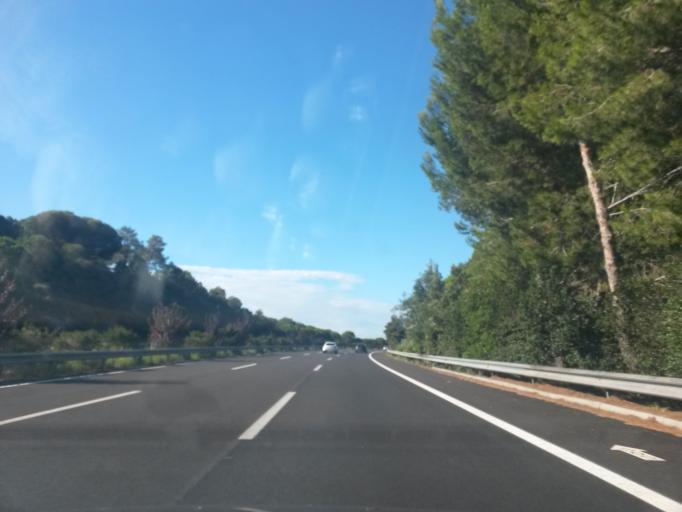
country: ES
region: Catalonia
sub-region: Provincia de Barcelona
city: Calella
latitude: 41.6359
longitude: 2.6715
